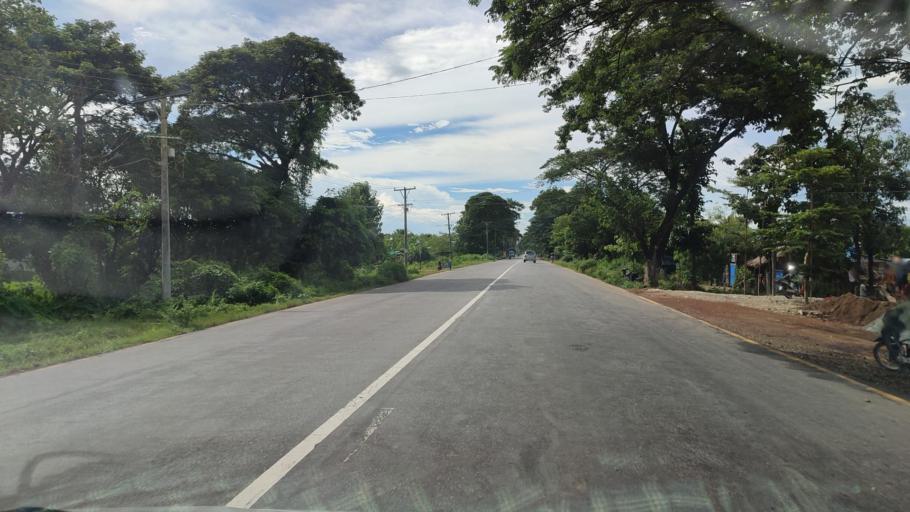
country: MM
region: Bago
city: Pyu
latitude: 18.3234
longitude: 96.4993
